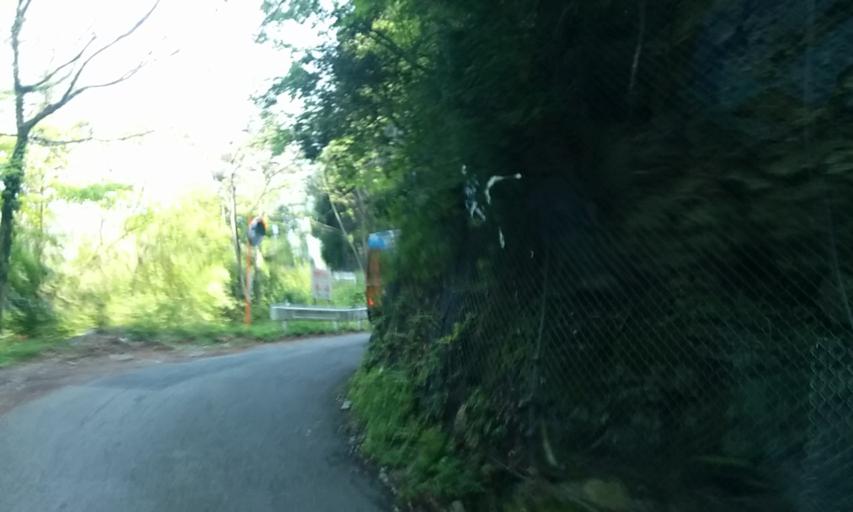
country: JP
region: Ehime
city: Niihama
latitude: 33.8699
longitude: 133.2944
